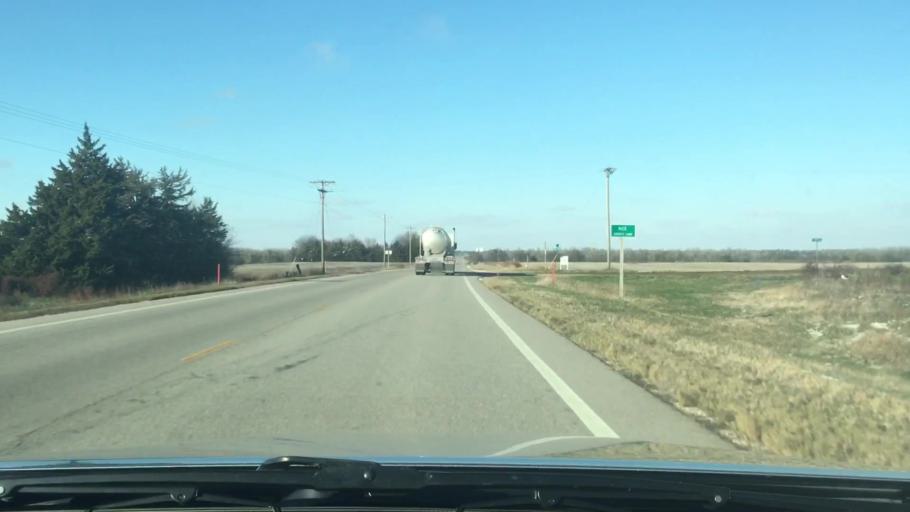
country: US
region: Kansas
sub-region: Rice County
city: Sterling
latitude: 38.1584
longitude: -98.2068
